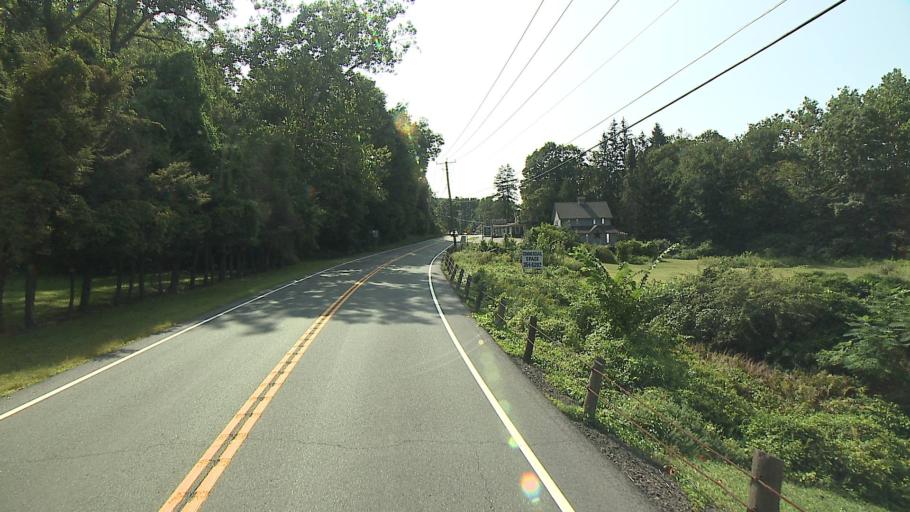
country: US
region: Connecticut
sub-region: Fairfield County
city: Sherman
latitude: 41.6497
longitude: -73.4854
